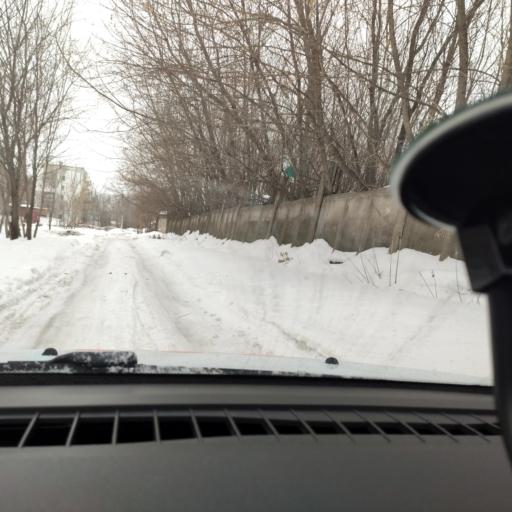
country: RU
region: Samara
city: Smyshlyayevka
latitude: 53.2503
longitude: 50.3780
